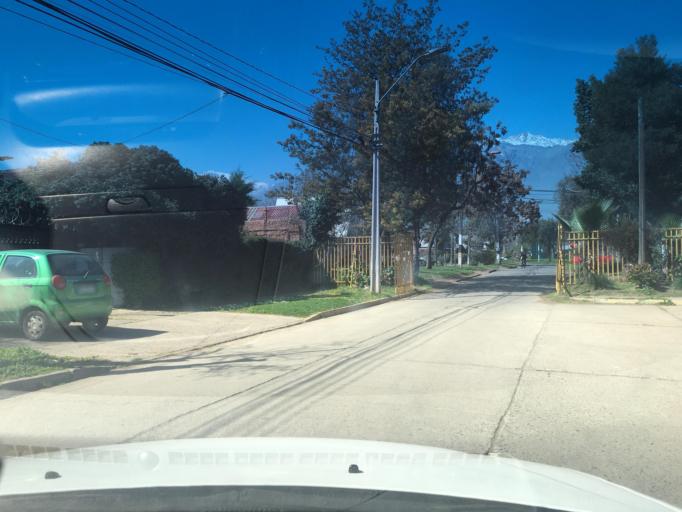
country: CL
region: Santiago Metropolitan
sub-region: Provincia de Santiago
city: Villa Presidente Frei, Nunoa, Santiago, Chile
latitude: -33.4682
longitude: -70.5706
